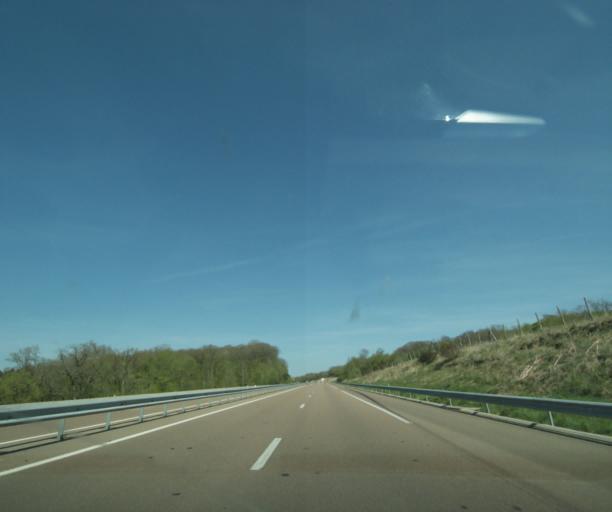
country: FR
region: Bourgogne
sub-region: Departement de la Nievre
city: Magny-Cours
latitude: 46.9156
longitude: 3.1611
